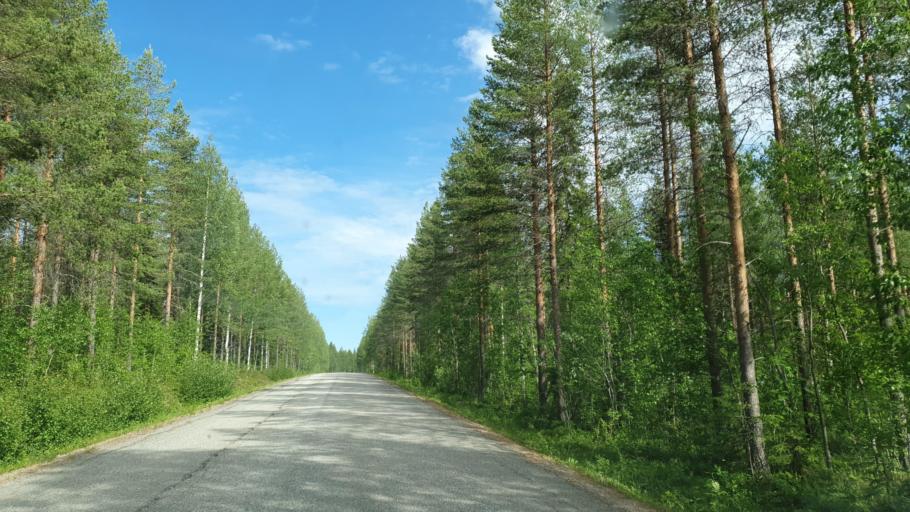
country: FI
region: Kainuu
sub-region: Kehys-Kainuu
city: Kuhmo
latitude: 64.5377
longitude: 29.3039
